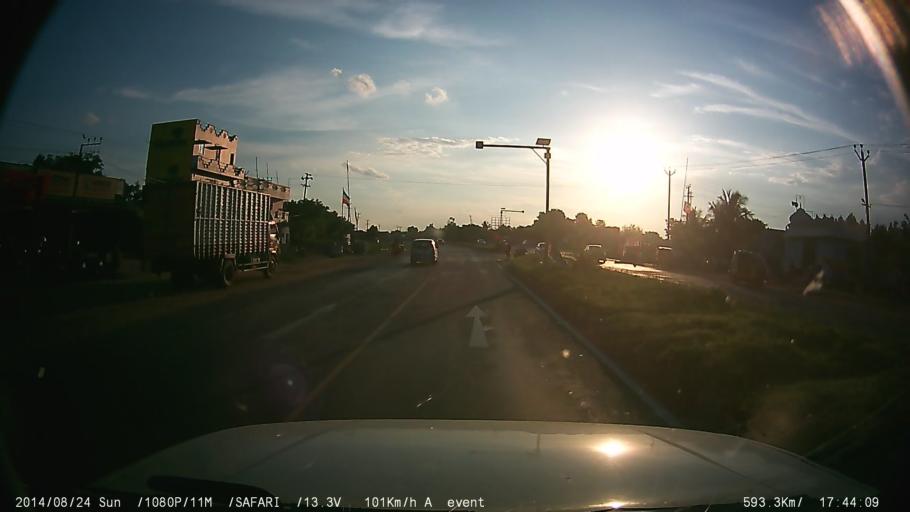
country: IN
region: Tamil Nadu
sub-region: Kancheepuram
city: Wallajahbad
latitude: 12.9040
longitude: 79.8194
